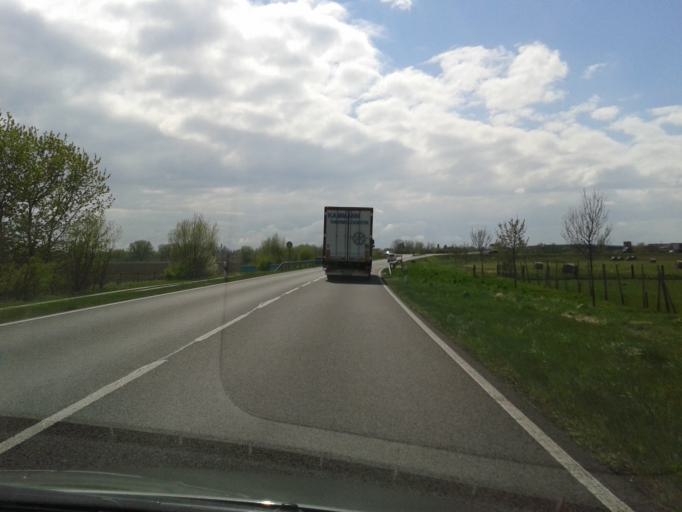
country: DE
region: Saxony-Anhalt
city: Salzwedel
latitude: 52.8619
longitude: 11.1763
